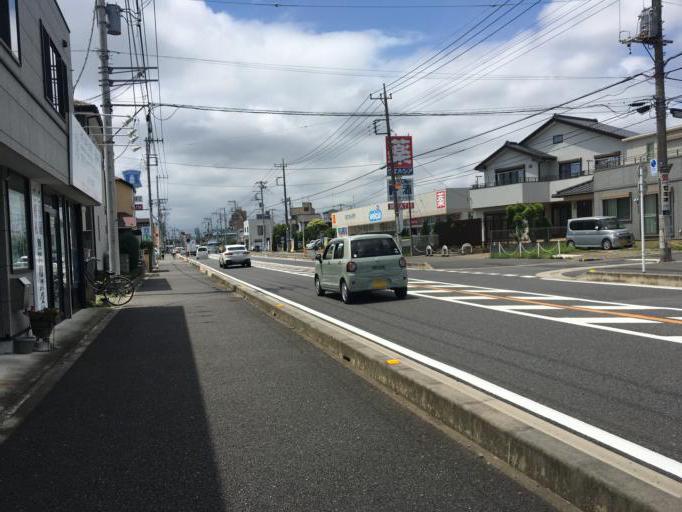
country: JP
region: Saitama
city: Okegawa
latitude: 35.9946
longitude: 139.5724
